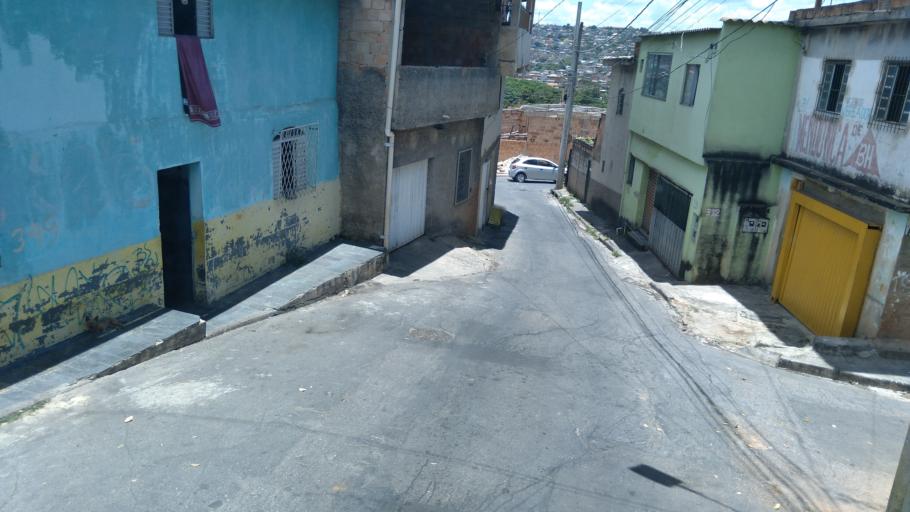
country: BR
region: Minas Gerais
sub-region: Santa Luzia
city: Santa Luzia
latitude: -19.8424
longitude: -43.8972
